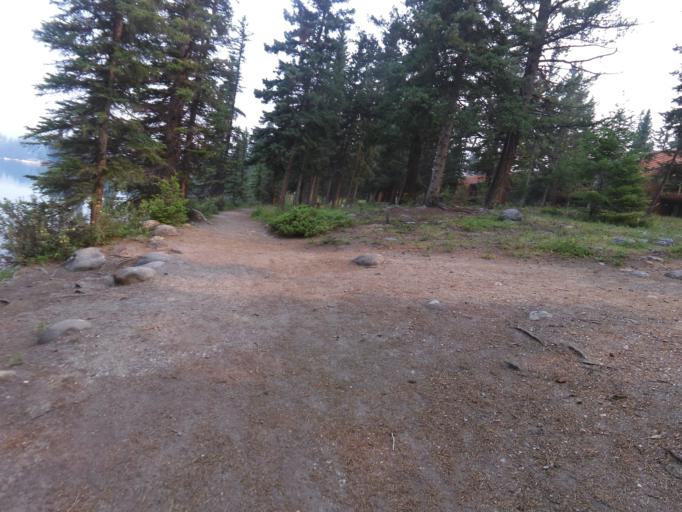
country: CA
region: Alberta
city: Jasper Park Lodge
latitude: 52.8829
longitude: -118.0535
